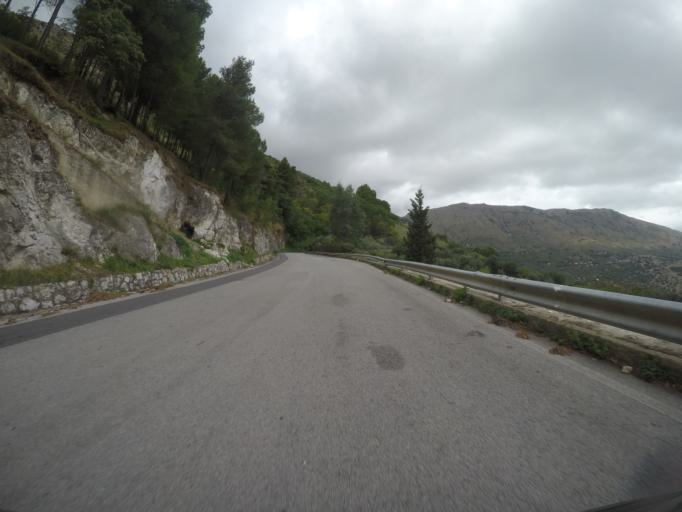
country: IT
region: Sicily
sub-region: Palermo
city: Montelepre
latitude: 38.1190
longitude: 13.1804
